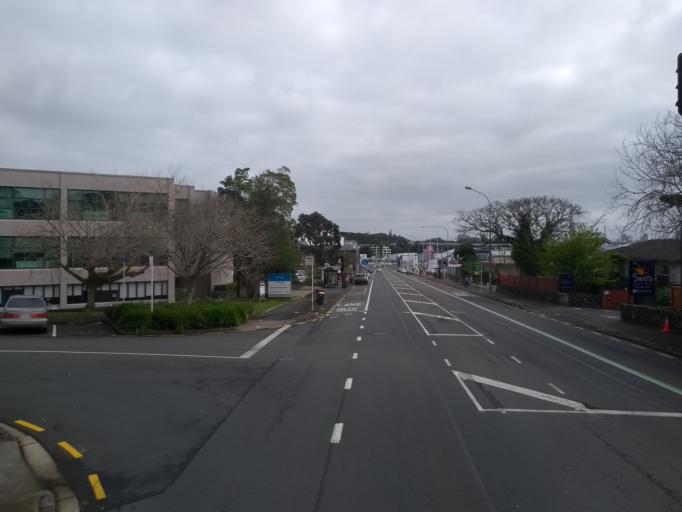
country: NZ
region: Auckland
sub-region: Auckland
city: Auckland
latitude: -36.8781
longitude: 174.7806
